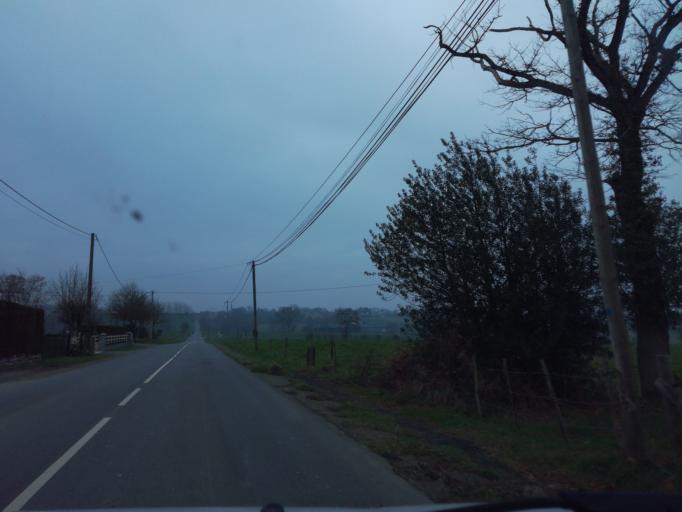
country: FR
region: Brittany
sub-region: Departement d'Ille-et-Vilaine
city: Gosne
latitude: 48.2577
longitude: -1.4531
